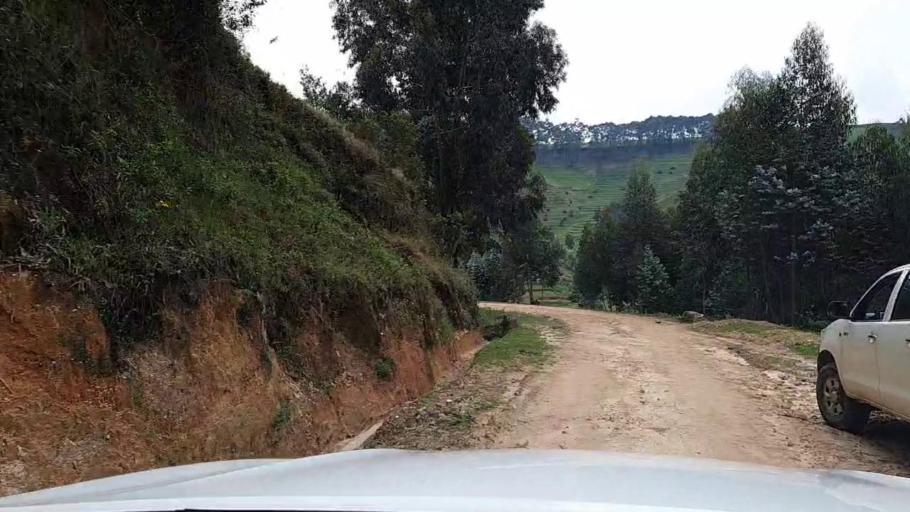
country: RW
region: Western Province
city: Kibuye
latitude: -2.2840
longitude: 29.3693
